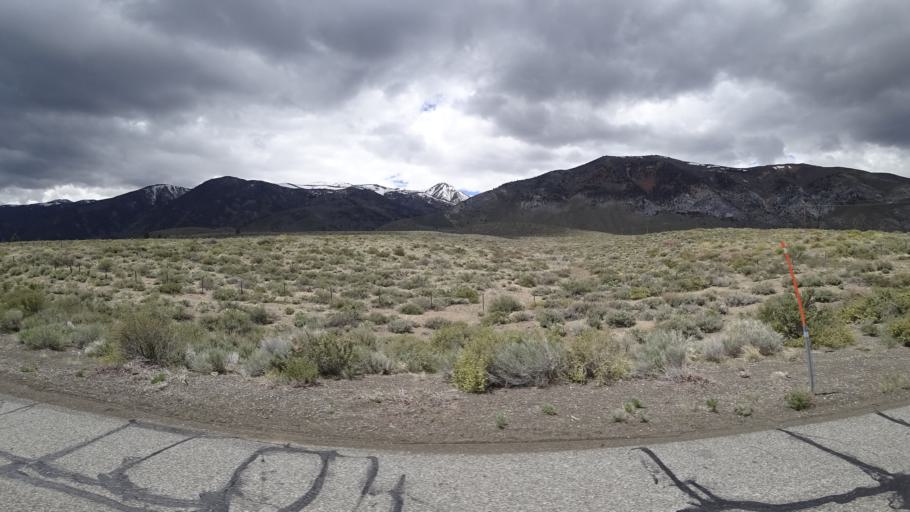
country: US
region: California
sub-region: Mono County
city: Bridgeport
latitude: 38.0446
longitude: -119.1603
